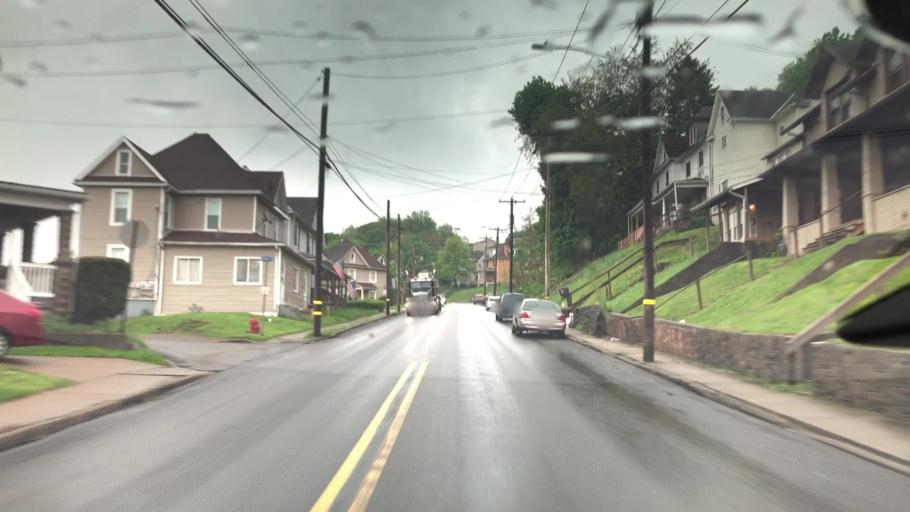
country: US
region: Pennsylvania
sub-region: Butler County
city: Butler
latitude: 40.8530
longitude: -79.8855
